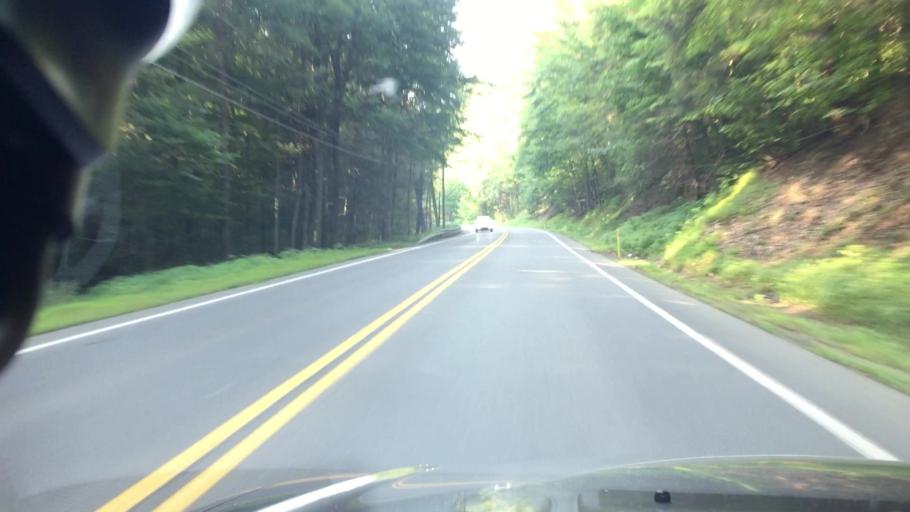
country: US
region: Pennsylvania
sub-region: Northumberland County
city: Elysburg
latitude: 40.8907
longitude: -76.5087
